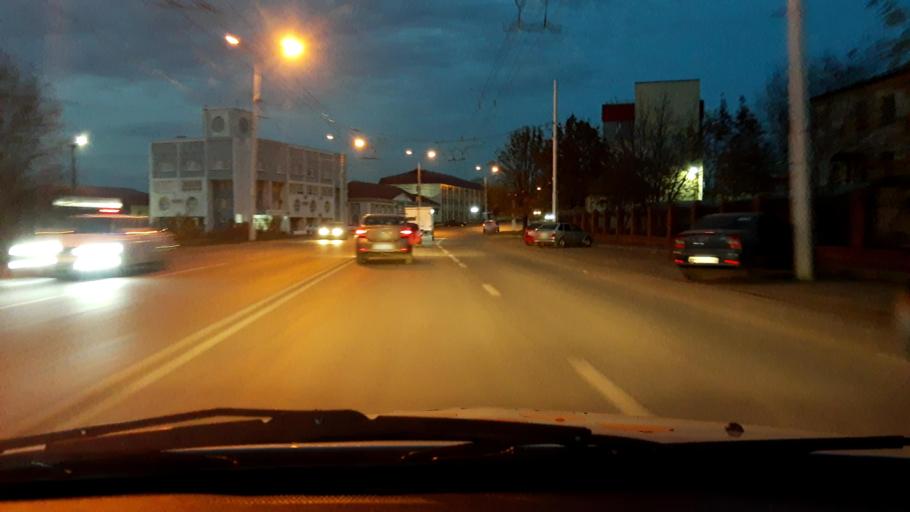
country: RU
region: Bashkortostan
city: Ufa
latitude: 54.8248
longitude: 56.0817
